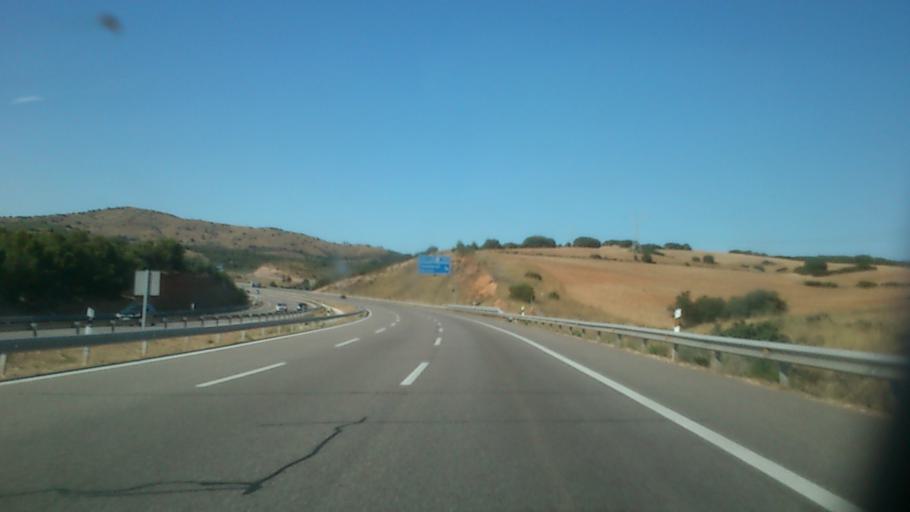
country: ES
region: Aragon
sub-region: Provincia de Zaragoza
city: Sediles
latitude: 41.3735
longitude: -1.5736
